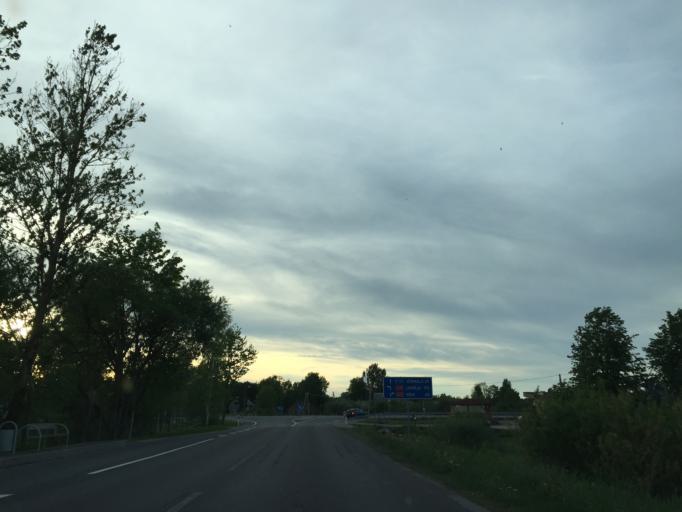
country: LV
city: Tireli
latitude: 56.8313
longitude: 23.5565
